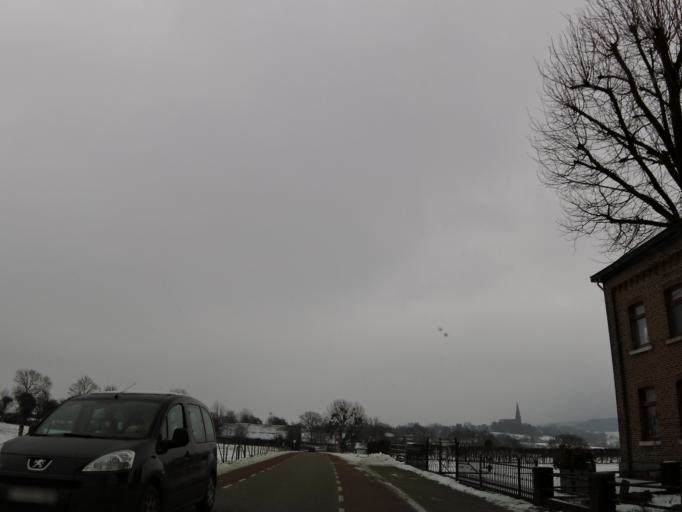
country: NL
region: Limburg
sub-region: Gemeente Simpelveld
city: Simpelveld
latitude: 50.7959
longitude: 5.9561
